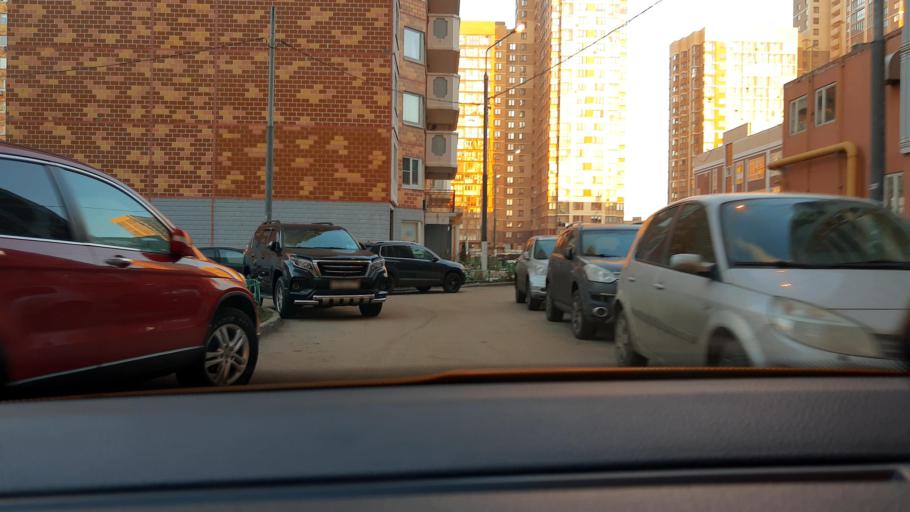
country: RU
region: Moskovskaya
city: Dolgoprudnyy
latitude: 55.9342
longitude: 37.5062
